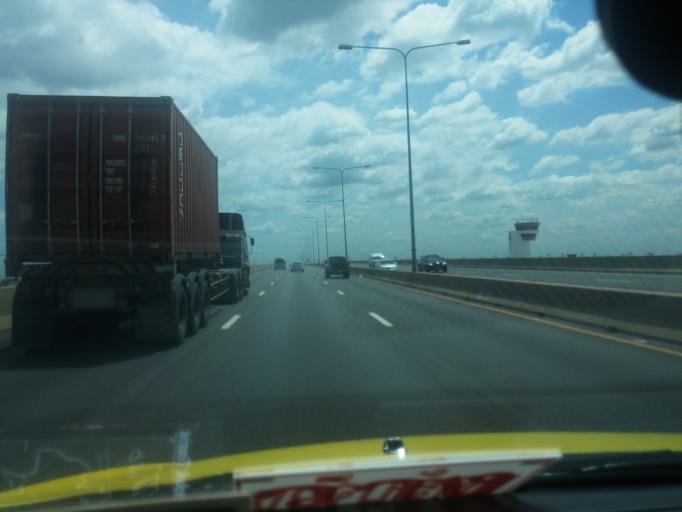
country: TH
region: Bangkok
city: Don Mueang
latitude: 13.9088
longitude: 100.5951
